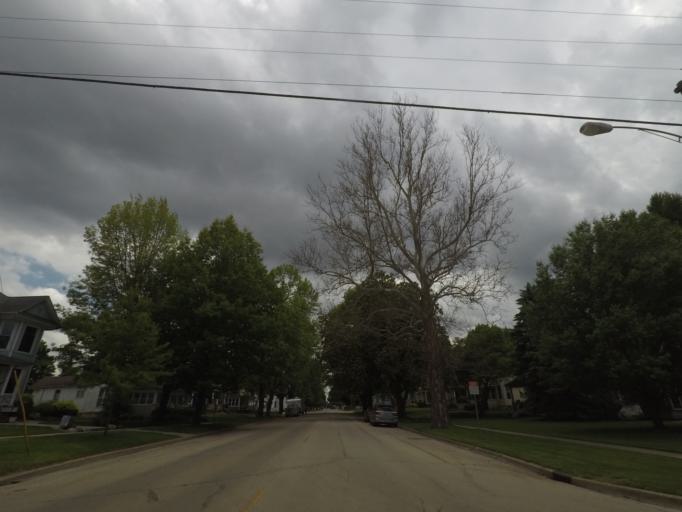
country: US
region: Illinois
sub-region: De Witt County
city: Clinton
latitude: 40.1582
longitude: -88.9606
